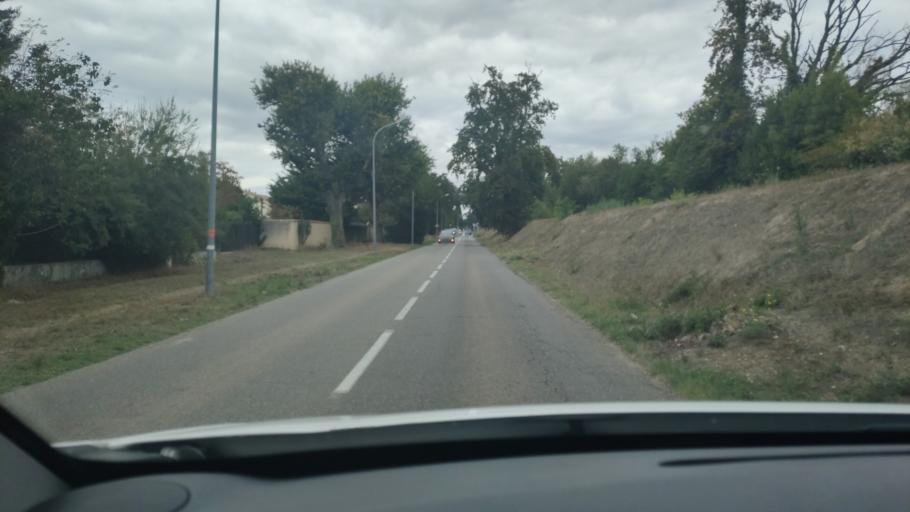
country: FR
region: Provence-Alpes-Cote d'Azur
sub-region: Departement du Vaucluse
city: Le Pontet
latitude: 43.9618
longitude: 4.8830
